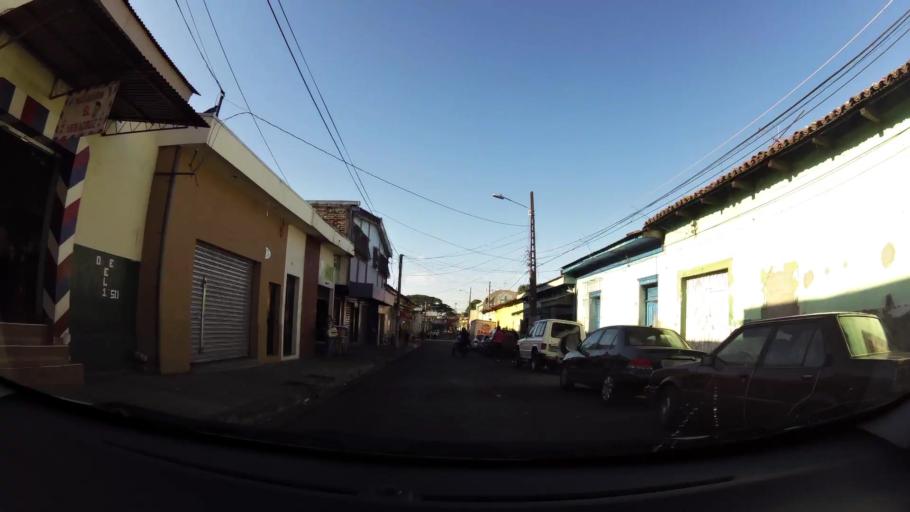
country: SV
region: Sonsonate
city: Sonsonate
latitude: 13.7188
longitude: -89.7288
